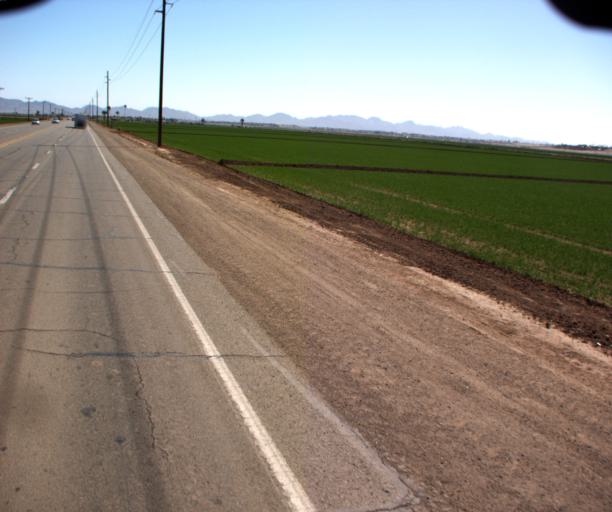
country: US
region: Arizona
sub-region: Yuma County
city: Yuma
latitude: 32.6988
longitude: -114.5725
